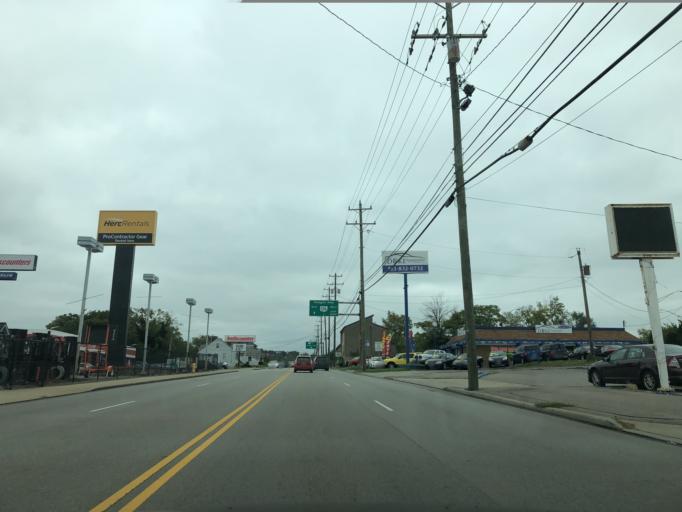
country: US
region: Ohio
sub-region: Hamilton County
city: Reading
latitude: 39.2119
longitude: -84.4532
